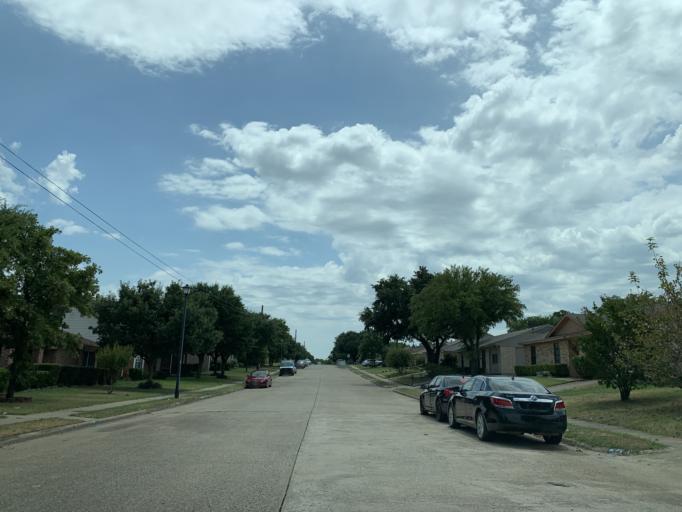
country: US
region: Texas
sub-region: Dallas County
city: DeSoto
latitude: 32.6610
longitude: -96.8123
